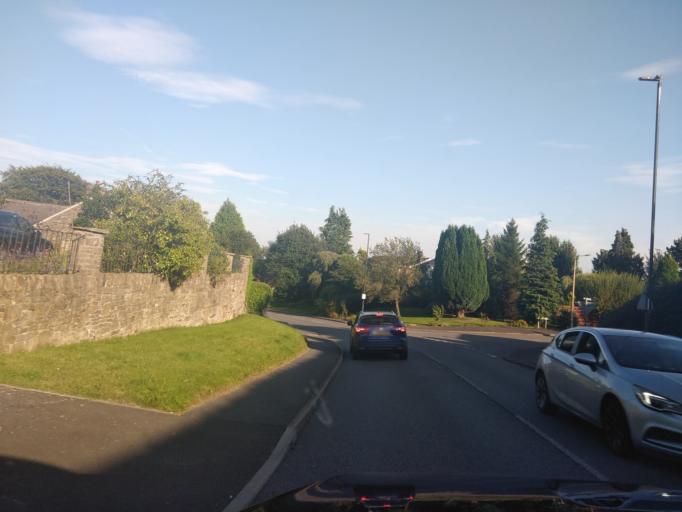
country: GB
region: England
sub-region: Derbyshire
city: Dronfield
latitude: 53.3028
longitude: -1.5051
